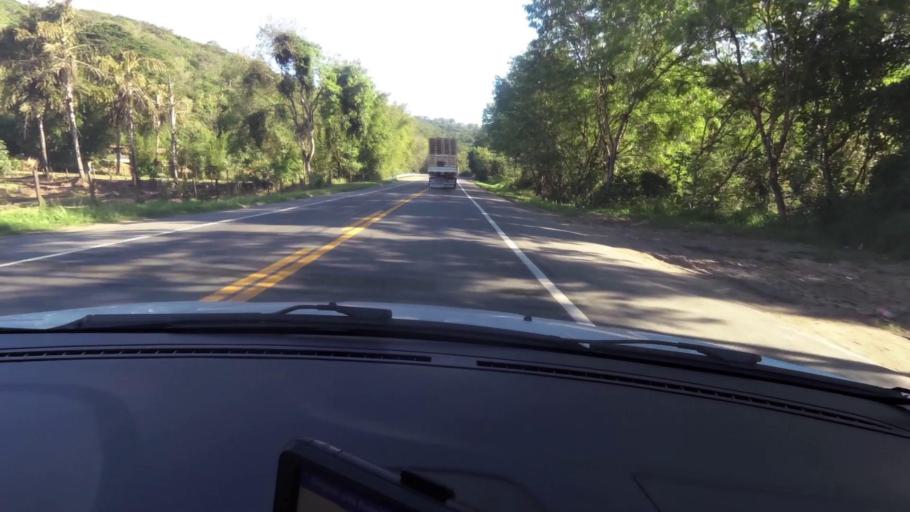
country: BR
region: Espirito Santo
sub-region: Alfredo Chaves
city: Alfredo Chaves
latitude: -20.6631
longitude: -40.6525
